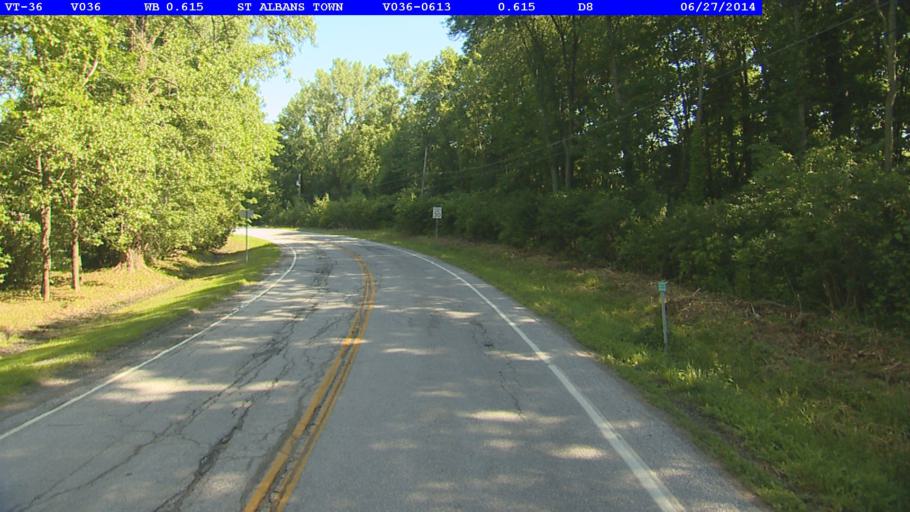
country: US
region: Vermont
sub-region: Franklin County
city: Saint Albans
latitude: 44.8094
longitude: -73.1406
